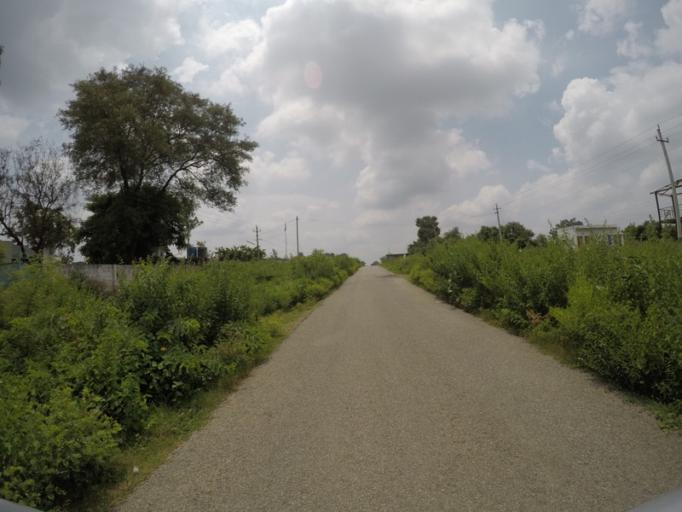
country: IN
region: Karnataka
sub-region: Ramanagara
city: Kanakapura
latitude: 12.7044
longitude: 77.4721
